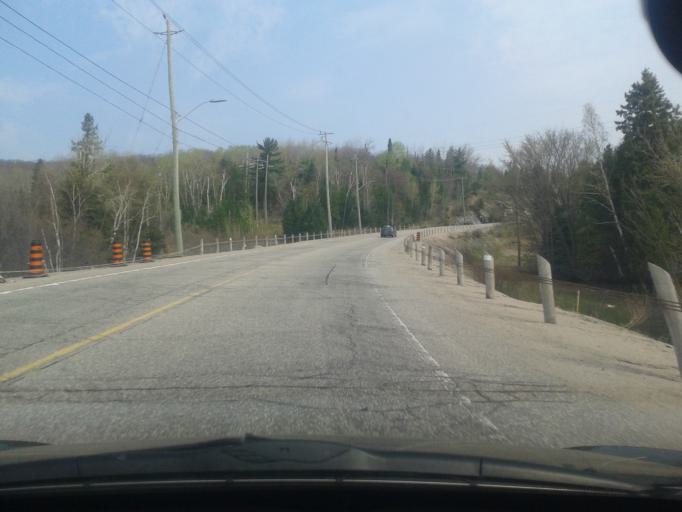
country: CA
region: Ontario
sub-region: Nipissing District
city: North Bay
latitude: 46.3357
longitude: -79.4939
